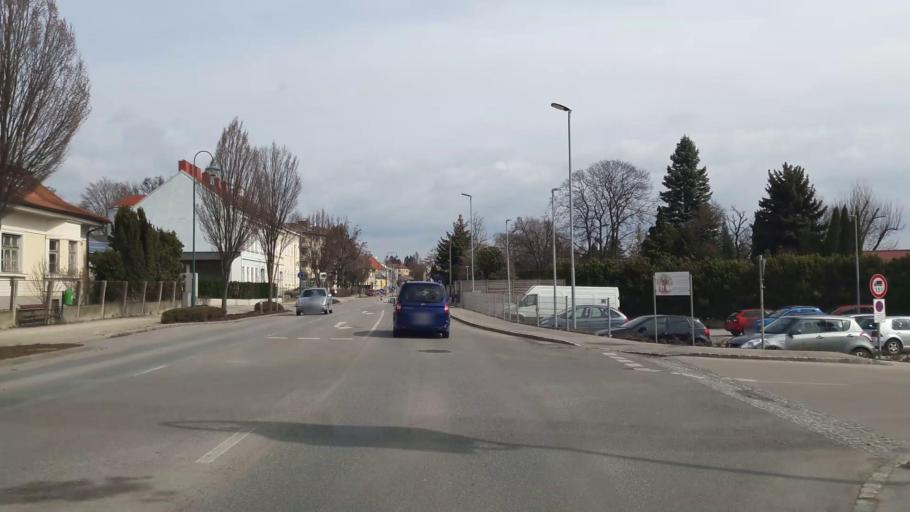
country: AT
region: Lower Austria
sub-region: Politischer Bezirk Mistelbach
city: Mistelbach
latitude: 48.5638
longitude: 16.5638
